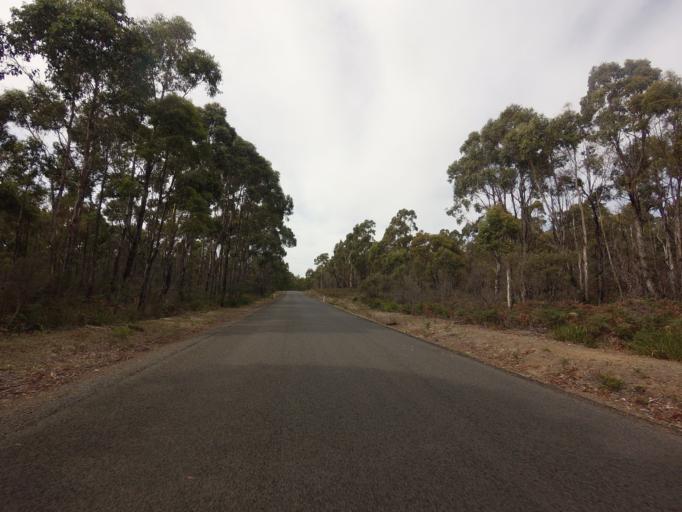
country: AU
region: Tasmania
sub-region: Sorell
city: Sorell
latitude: -42.5187
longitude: 147.6496
